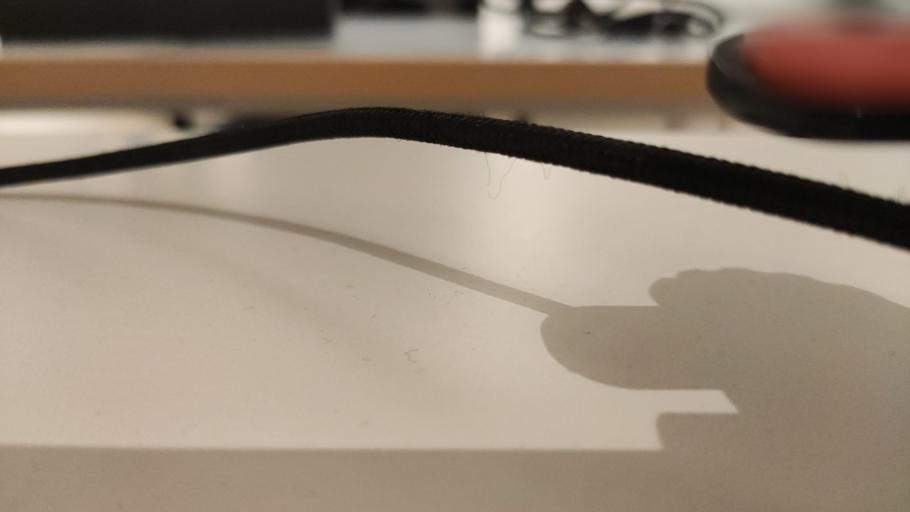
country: RU
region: Moskovskaya
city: Dorokhovo
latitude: 55.4631
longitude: 36.3546
